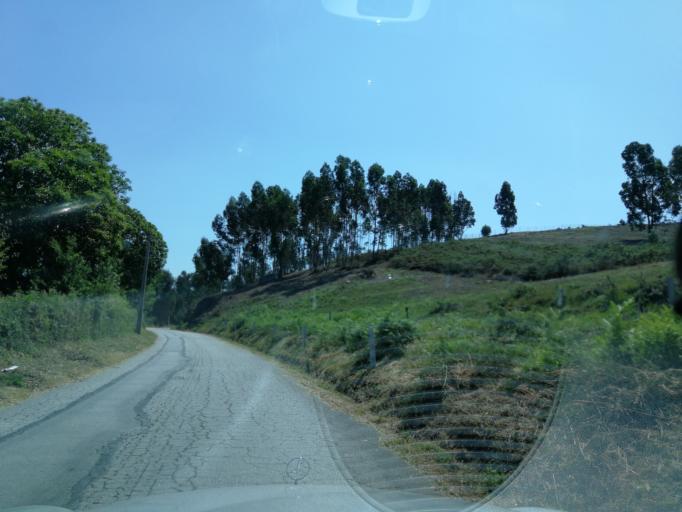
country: PT
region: Braga
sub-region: Povoa de Lanhoso
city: Povoa de Lanhoso
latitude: 41.5816
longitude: -8.3227
